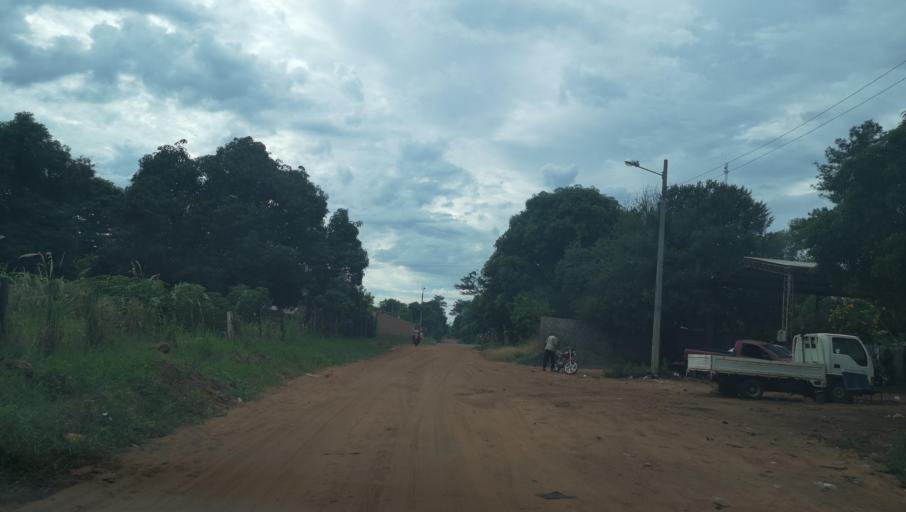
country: PY
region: San Pedro
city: Capiibary
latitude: -24.7440
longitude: -56.0273
